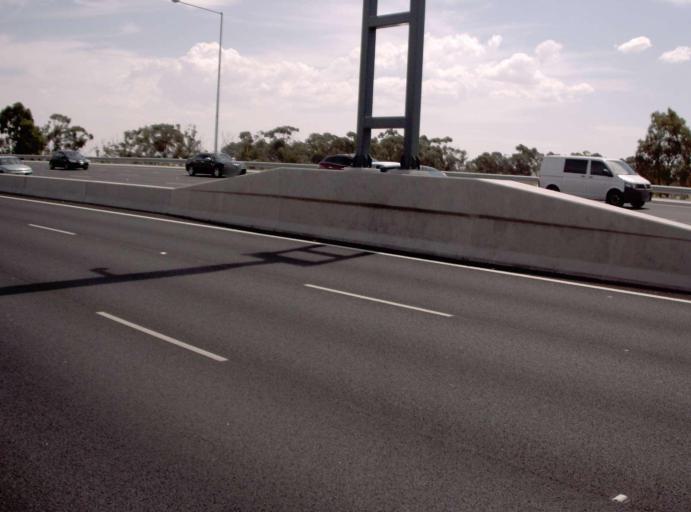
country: AU
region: Victoria
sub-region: Brimbank
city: Cairnlea
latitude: -37.7676
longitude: 144.8005
